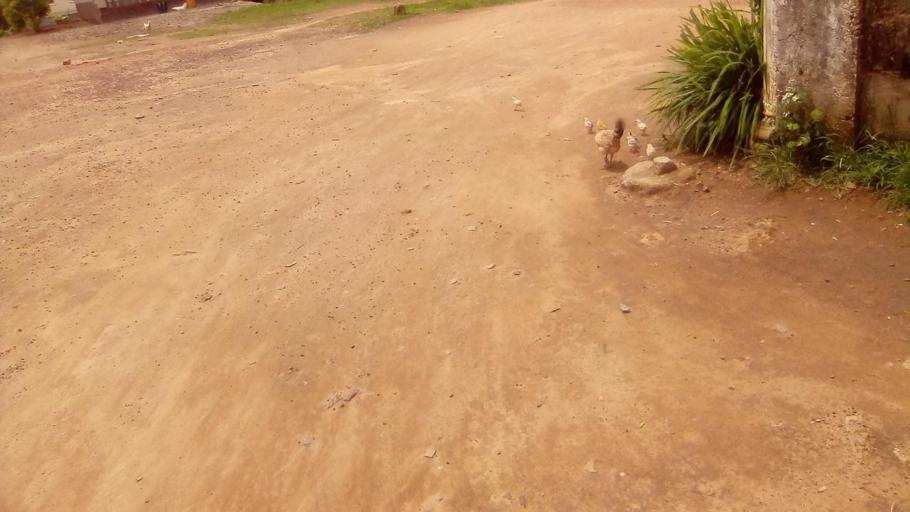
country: SL
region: Southern Province
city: Bo
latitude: 7.9375
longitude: -11.7377
